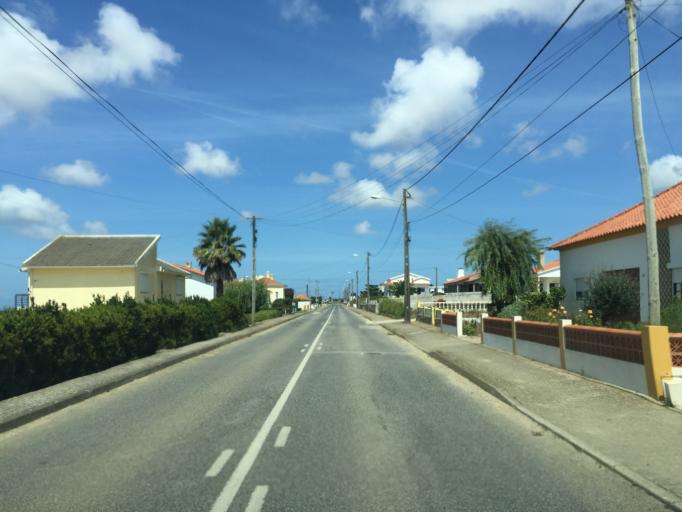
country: PT
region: Lisbon
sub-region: Lourinha
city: Lourinha
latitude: 39.2814
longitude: -9.3013
